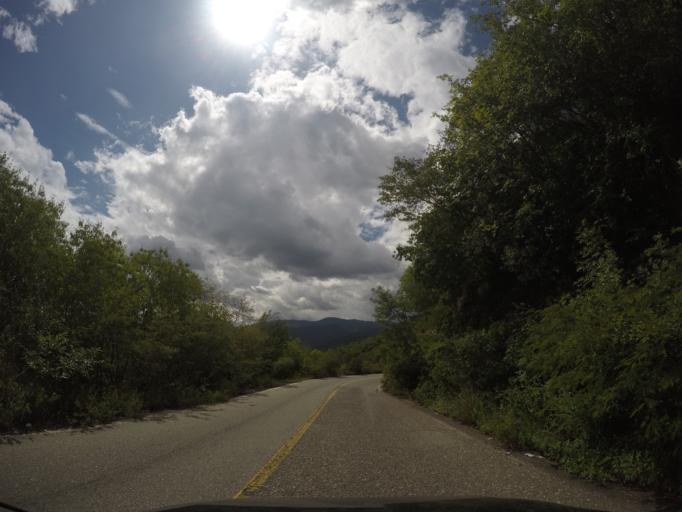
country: MX
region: Oaxaca
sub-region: San Jeronimo Coatlan
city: San Cristobal Honduras
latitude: 16.4316
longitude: -97.0463
